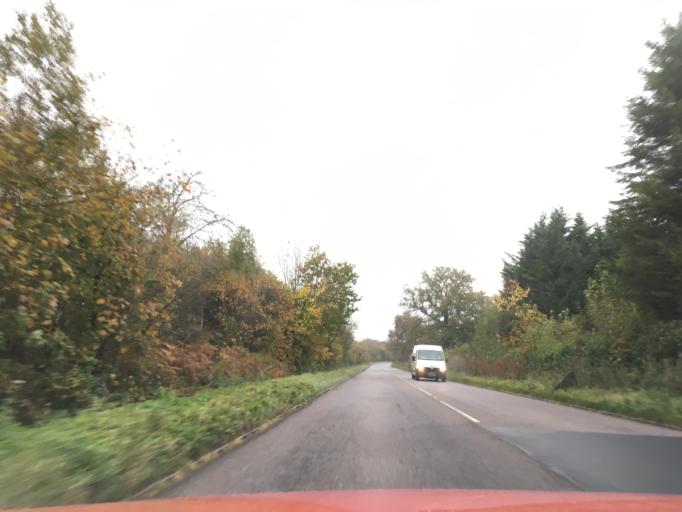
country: GB
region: England
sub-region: West Berkshire
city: Wickham
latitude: 51.4396
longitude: -1.4234
